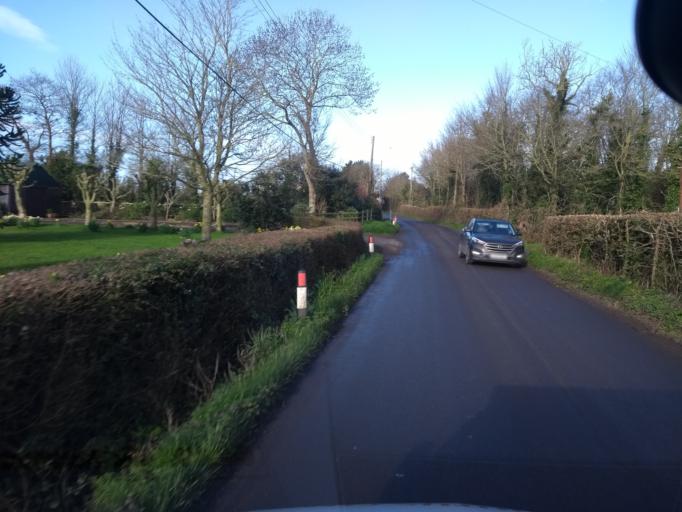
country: GB
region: England
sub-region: Somerset
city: Woolavington
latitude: 51.1570
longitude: -2.9028
